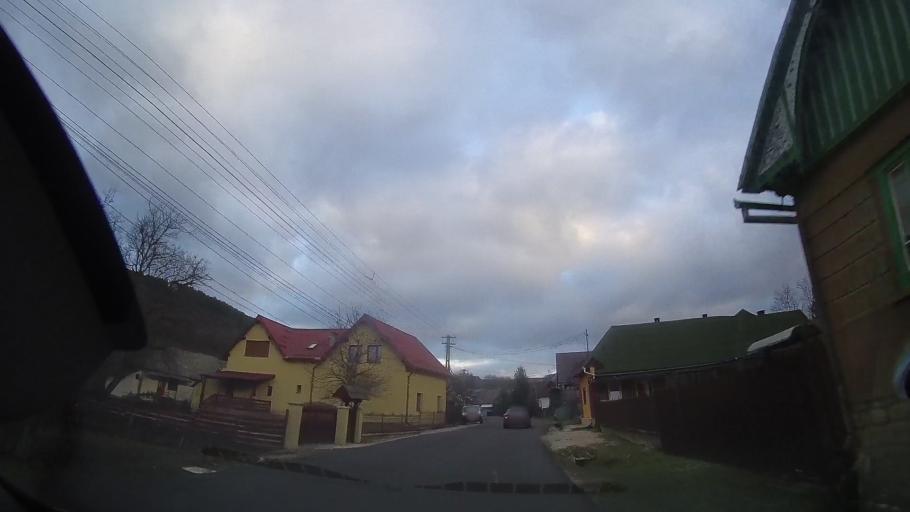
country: RO
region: Cluj
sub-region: Comuna Calatele
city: Calatele
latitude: 46.7820
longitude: 23.0267
